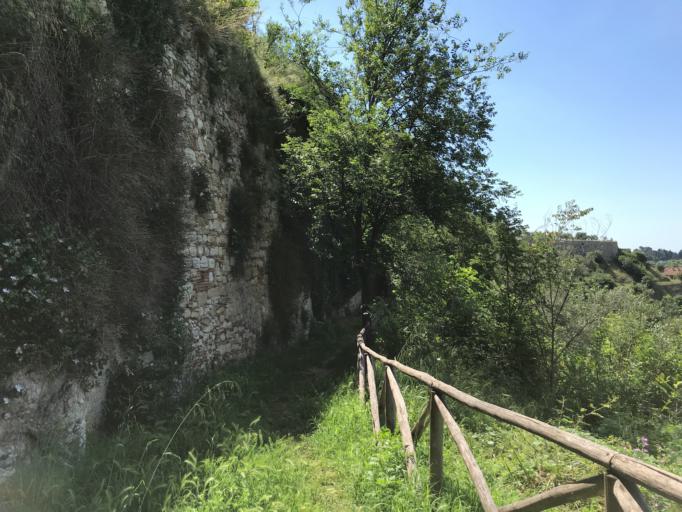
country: IT
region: Umbria
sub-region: Provincia di Terni
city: Amelia
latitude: 42.5572
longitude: 12.4116
